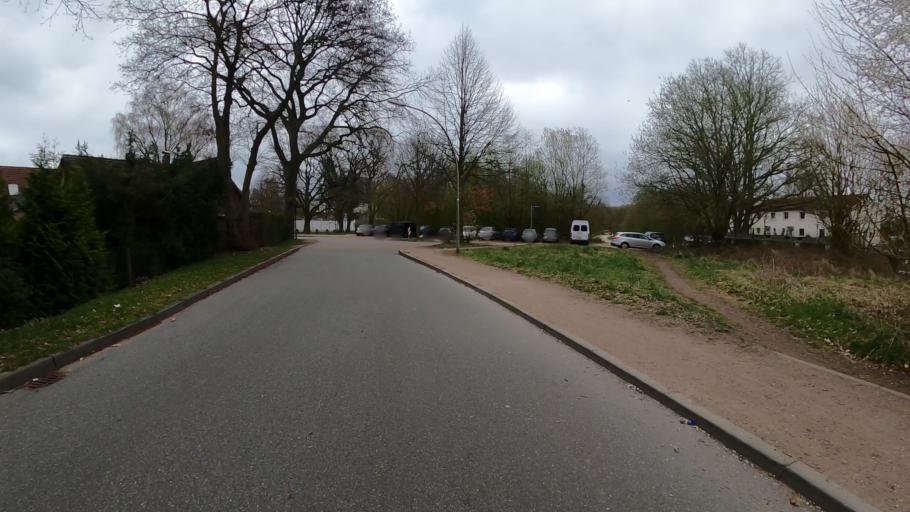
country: DE
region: Hamburg
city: Langenhorn
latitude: 53.6554
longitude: 9.9979
